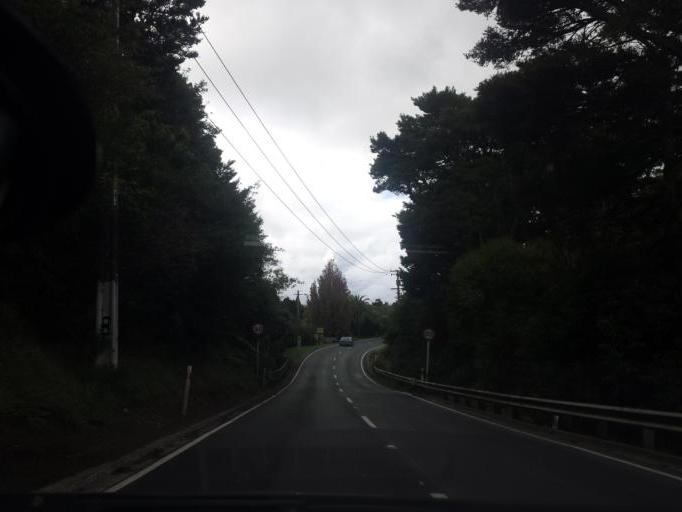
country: NZ
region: Auckland
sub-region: Auckland
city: Warkworth
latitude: -36.3953
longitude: 174.6616
